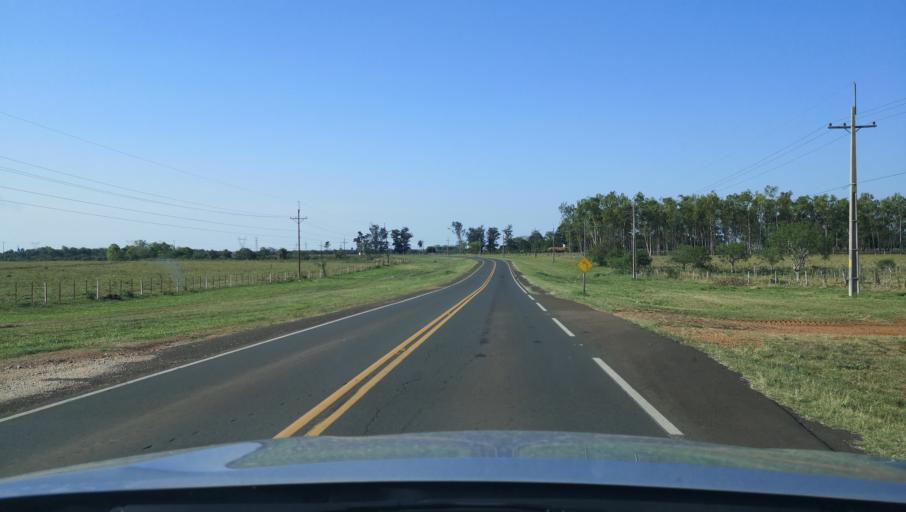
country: PY
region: Misiones
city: Santa Maria
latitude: -26.8101
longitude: -57.0212
